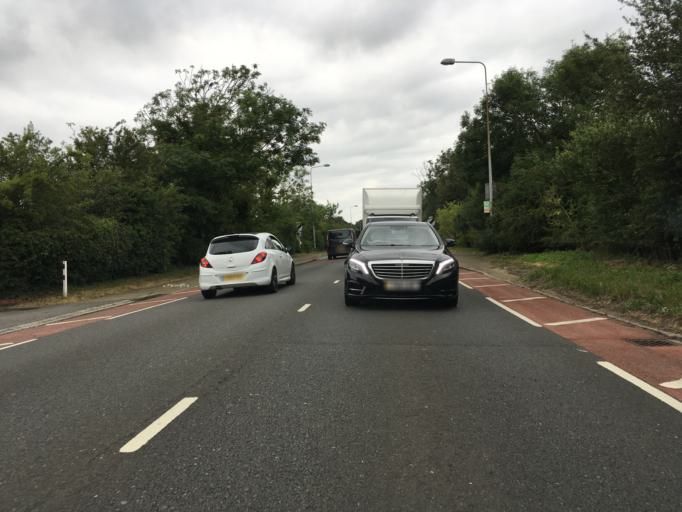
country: GB
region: England
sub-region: Central Bedfordshire
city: Hockliffe
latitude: 51.9339
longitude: -0.5908
